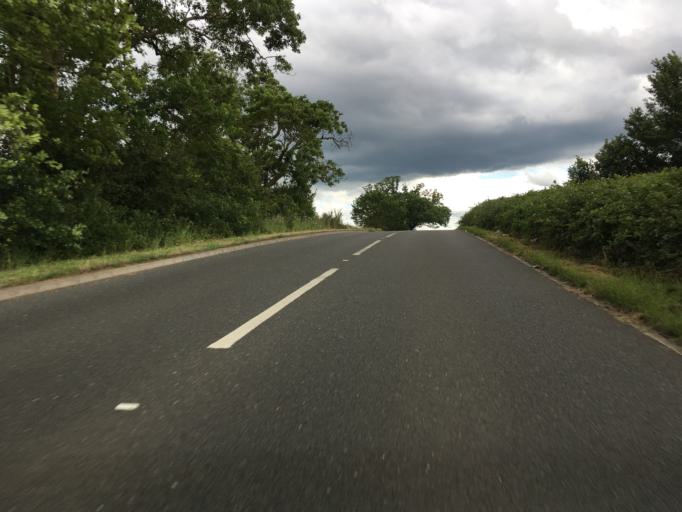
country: GB
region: England
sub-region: Central Bedfordshire
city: Leighton Buzzard
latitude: 51.9331
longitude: -0.6910
